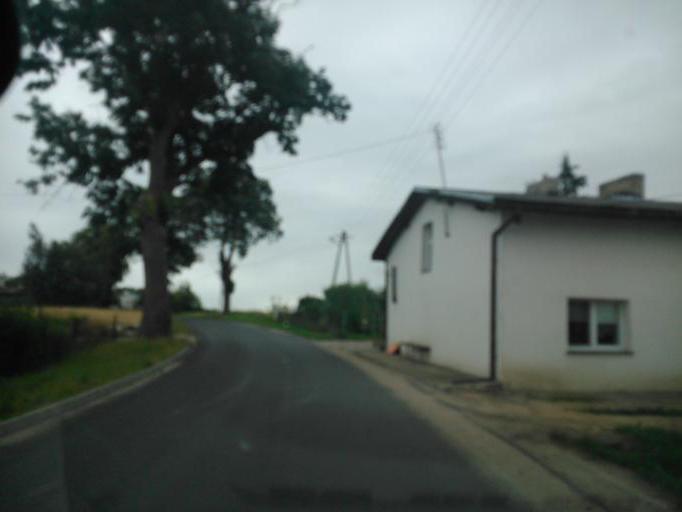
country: PL
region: Kujawsko-Pomorskie
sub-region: Powiat brodnicki
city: Jablonowo Pomorskie
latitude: 53.4011
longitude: 19.1433
